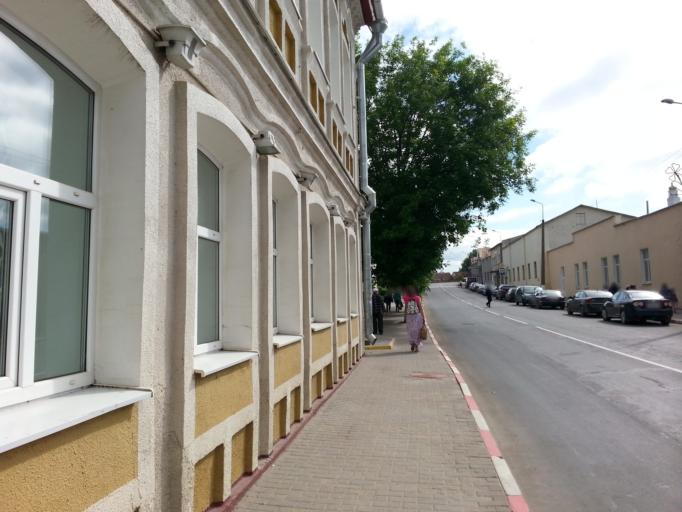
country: BY
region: Vitebsk
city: Hlybokaye
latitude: 55.1395
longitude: 27.6922
